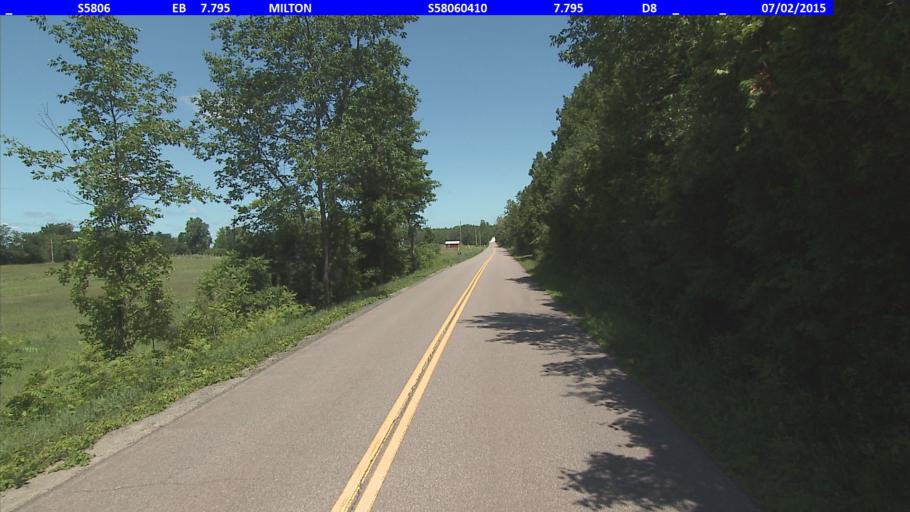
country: US
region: Vermont
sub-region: Chittenden County
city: Milton
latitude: 44.7083
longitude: -73.2057
